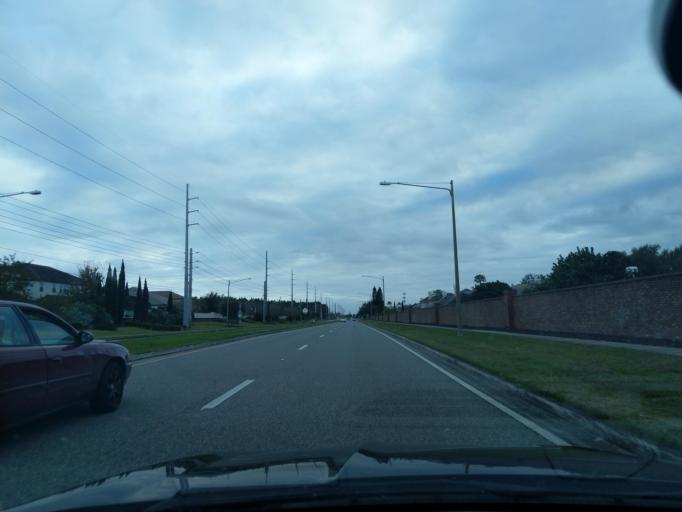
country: US
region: Florida
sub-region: Orange County
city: Doctor Phillips
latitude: 28.4134
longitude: -81.5033
